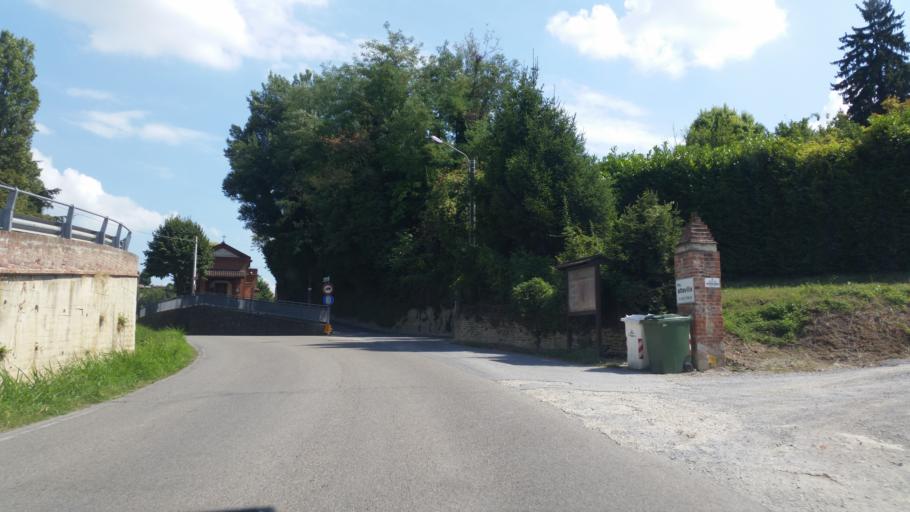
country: IT
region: Piedmont
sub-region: Provincia di Cuneo
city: Alba
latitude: 44.6946
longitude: 8.0488
